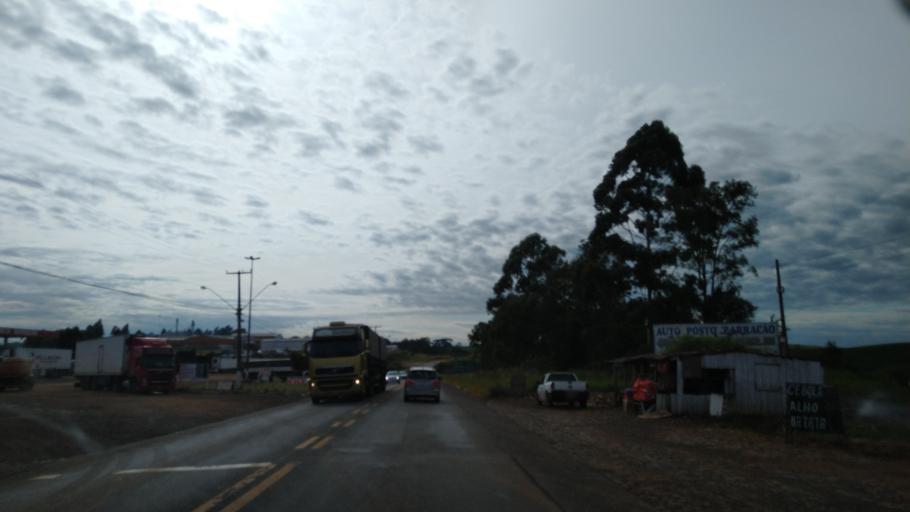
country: AR
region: Misiones
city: Bernardo de Irigoyen
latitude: -26.2601
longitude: -53.6140
